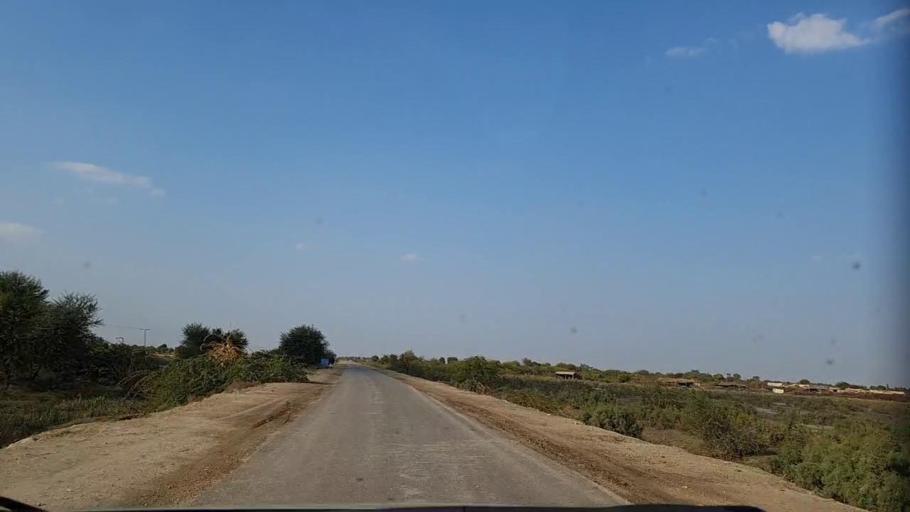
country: PK
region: Sindh
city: Pithoro
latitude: 25.6988
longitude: 69.2227
